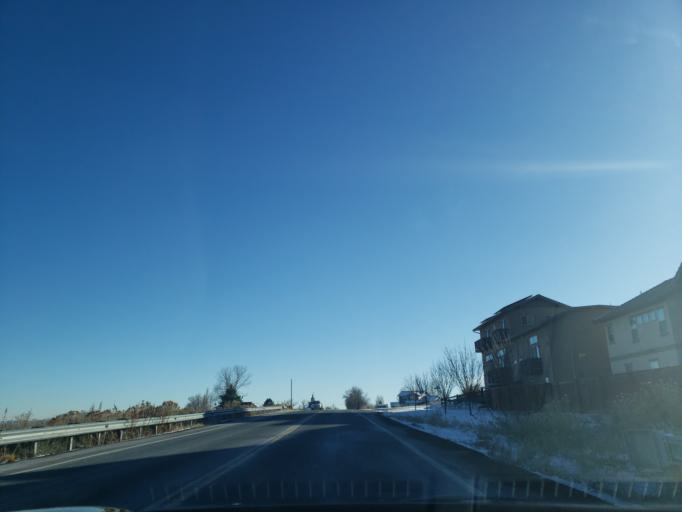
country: US
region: Colorado
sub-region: Weld County
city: Windsor
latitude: 40.5150
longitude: -105.0010
